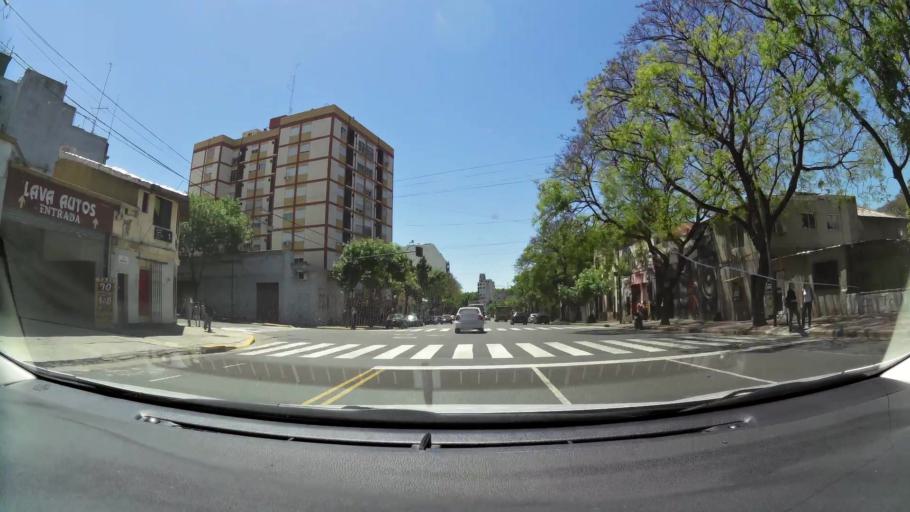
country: AR
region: Buenos Aires F.D.
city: Buenos Aires
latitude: -34.6332
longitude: -58.3867
